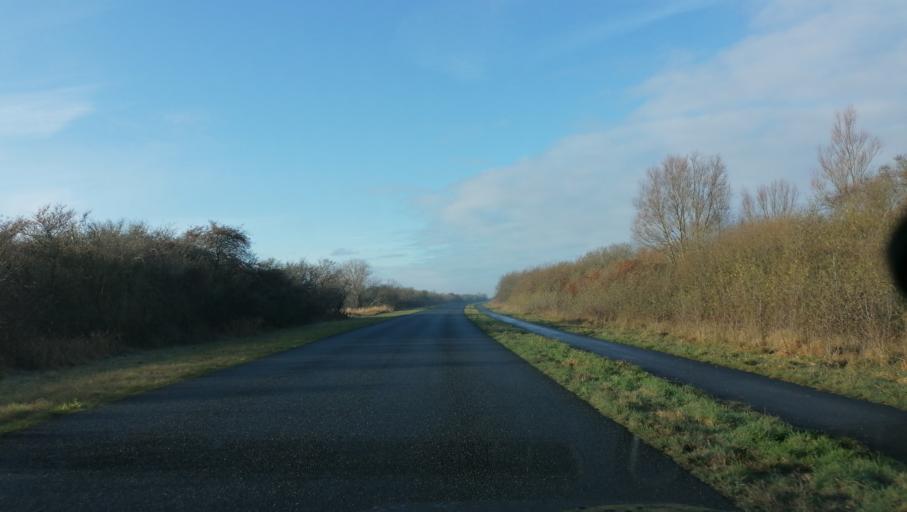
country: DE
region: Schleswig-Holstein
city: Elpersbuttel
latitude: 54.0926
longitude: 8.9848
